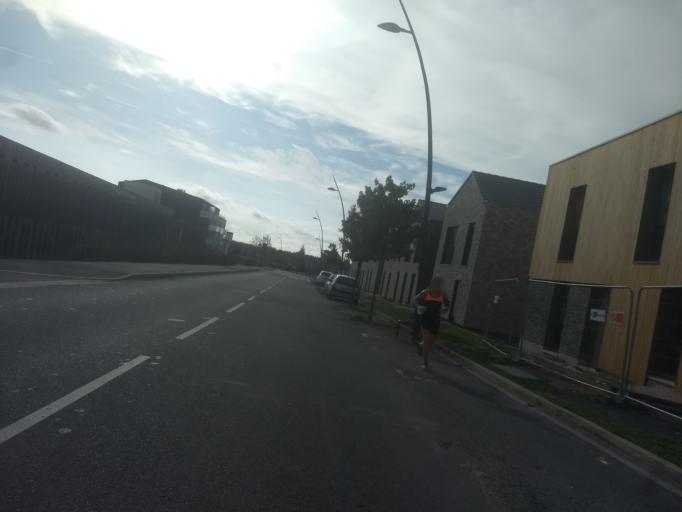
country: FR
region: Nord-Pas-de-Calais
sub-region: Departement du Pas-de-Calais
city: Dainville
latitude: 50.2903
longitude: 2.7359
